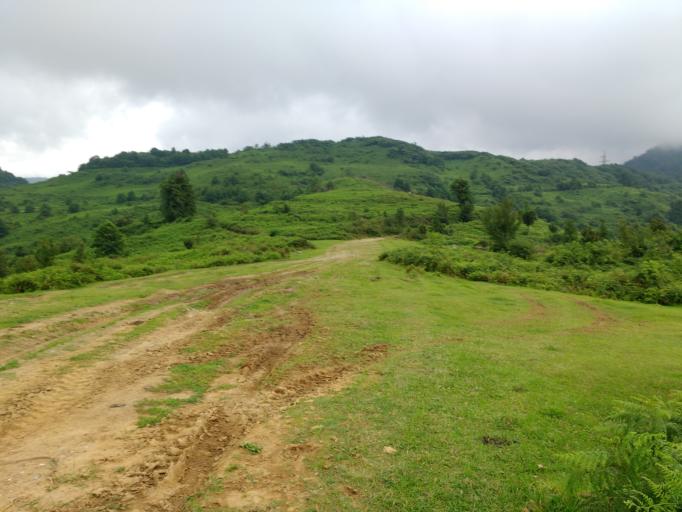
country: GE
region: Ajaria
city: Khelvachauri
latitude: 41.5602
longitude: 41.5850
